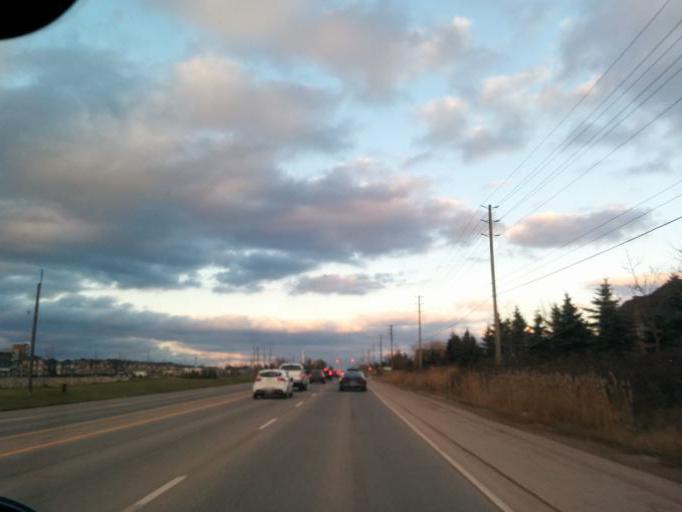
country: CA
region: Ontario
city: Oakville
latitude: 43.4724
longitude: -79.7366
